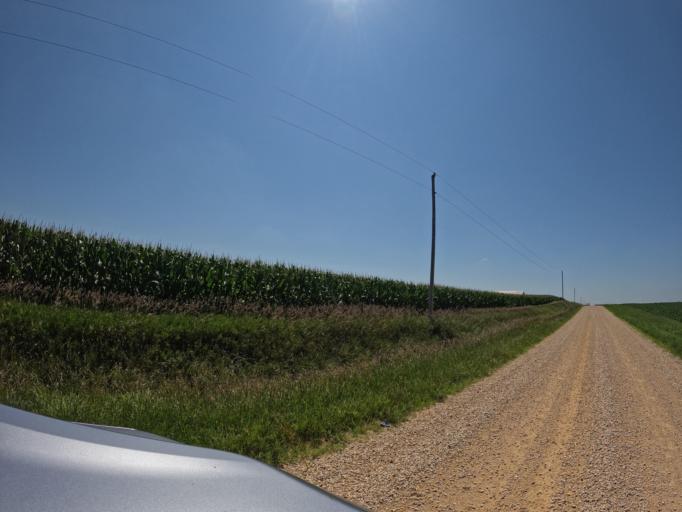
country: US
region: Iowa
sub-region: Clinton County
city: Camanche
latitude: 41.7932
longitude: -90.3937
